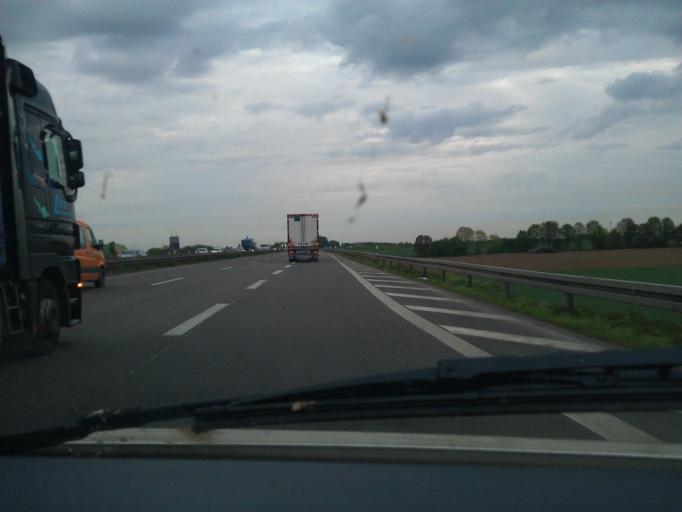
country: DE
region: North Rhine-Westphalia
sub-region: Regierungsbezirk Koln
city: Wurselen
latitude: 50.8087
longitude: 6.1716
